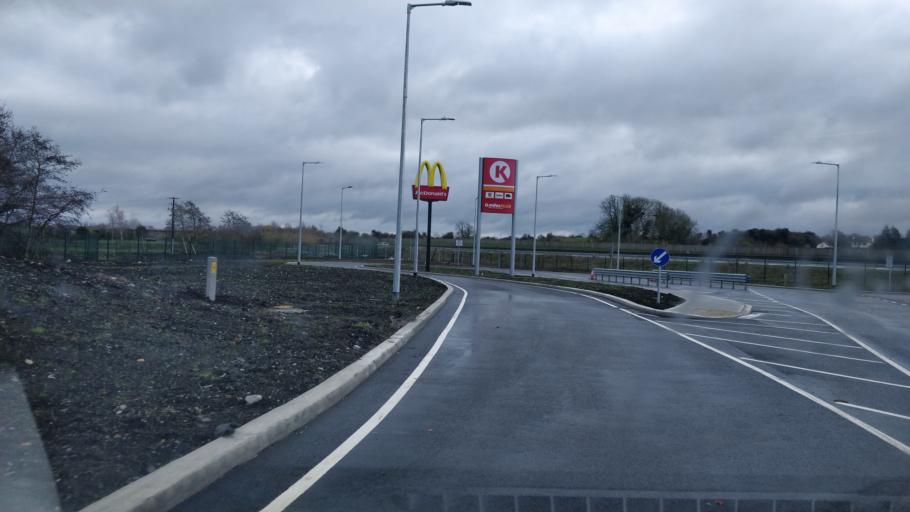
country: IE
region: Leinster
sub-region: An Iarmhi
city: Moate
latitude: 53.3997
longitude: -7.8265
